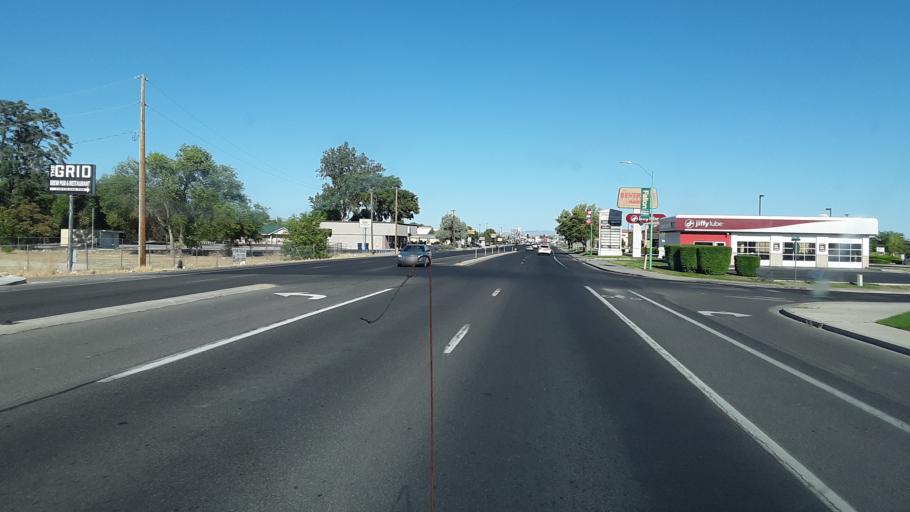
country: US
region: Nevada
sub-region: Churchill County
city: Fallon
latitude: 39.4775
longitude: -118.8056
